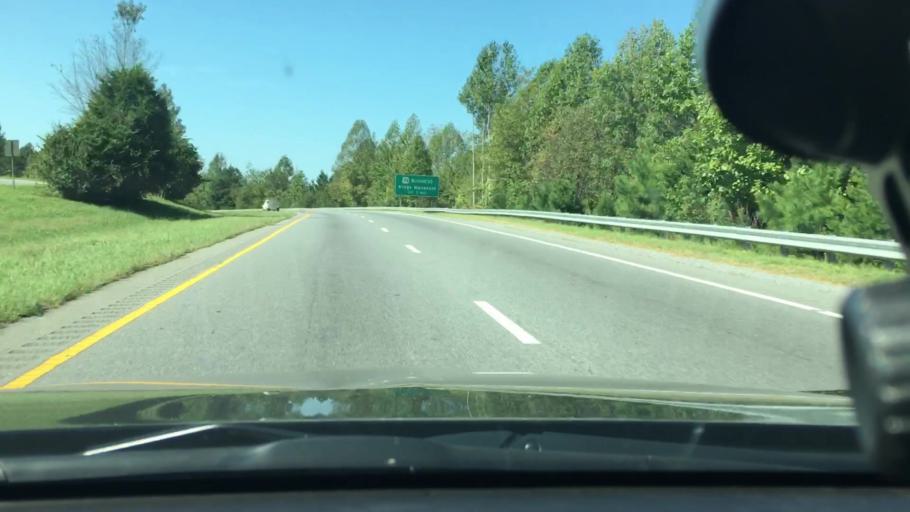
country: US
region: North Carolina
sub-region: Gaston County
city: Bessemer City
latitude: 35.2518
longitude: -81.2997
